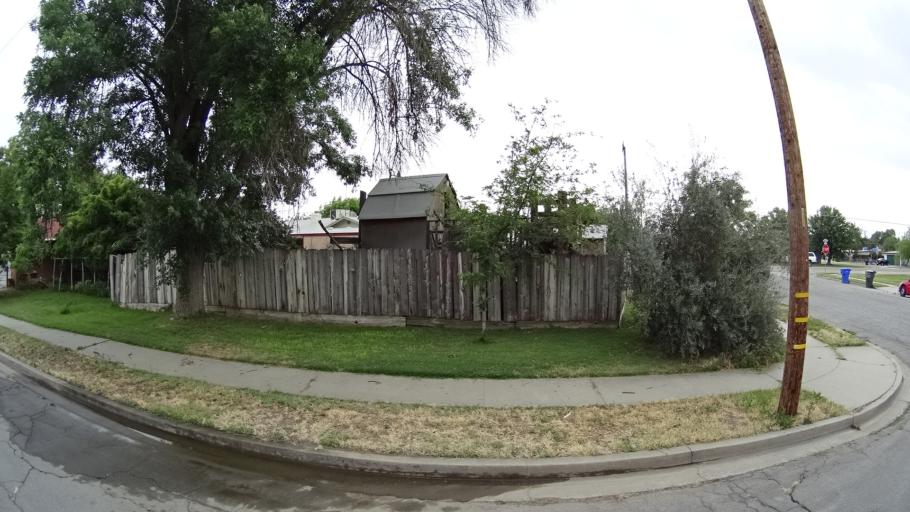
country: US
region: California
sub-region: Kings County
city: Hanford
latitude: 36.3411
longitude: -119.6601
